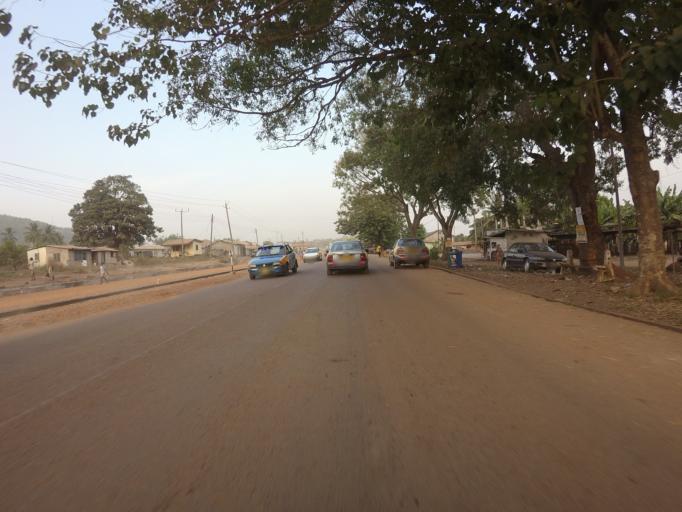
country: GH
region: Volta
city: Ho
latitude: 6.5964
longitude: 0.4438
